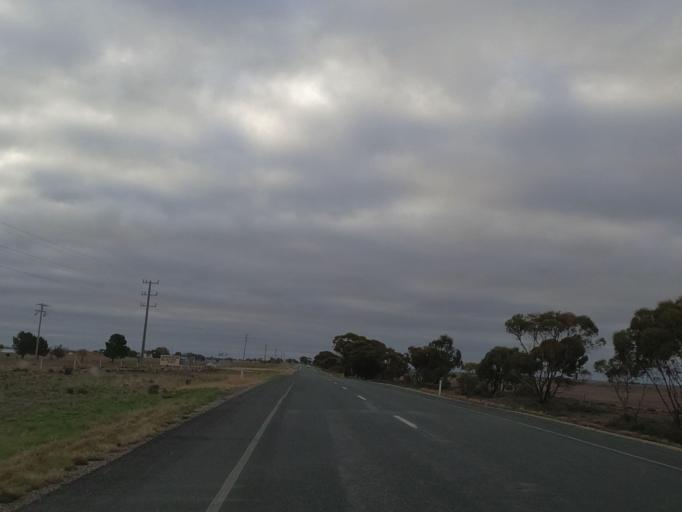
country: AU
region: Victoria
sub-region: Swan Hill
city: Swan Hill
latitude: -35.5834
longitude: 143.7900
